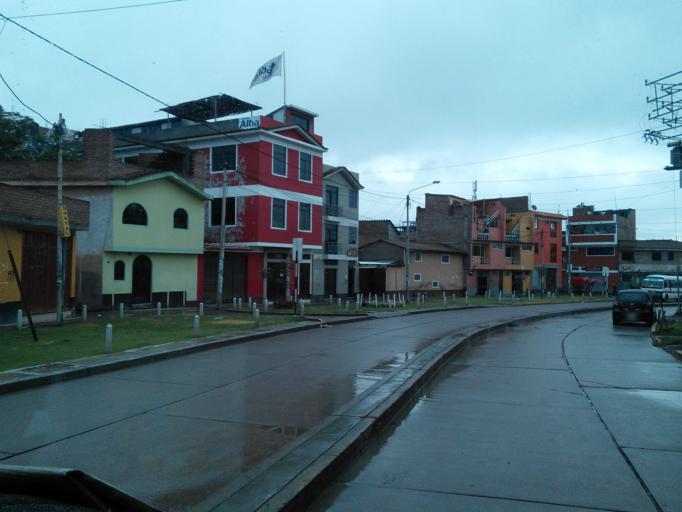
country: PE
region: Ayacucho
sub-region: Provincia de Huamanga
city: Ayacucho
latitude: -13.1653
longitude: -74.2246
